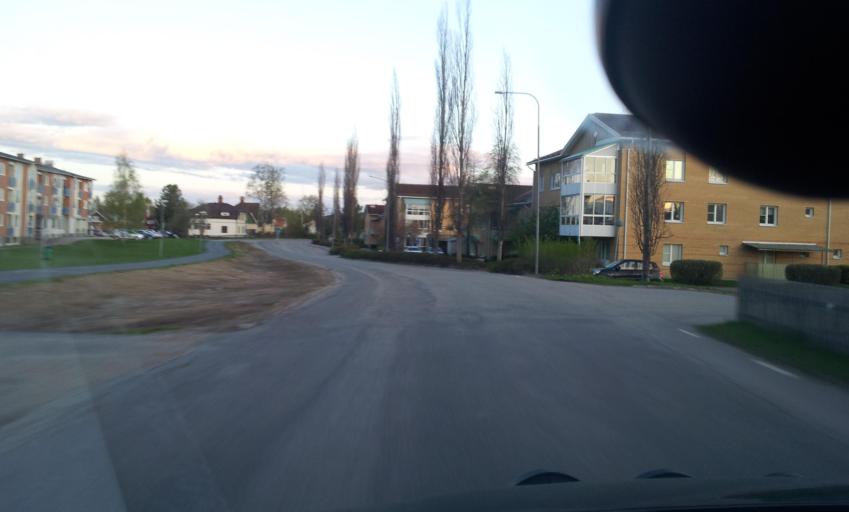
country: SE
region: Gaevleborg
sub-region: Bollnas Kommun
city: Bollnas
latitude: 61.3597
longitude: 16.4058
